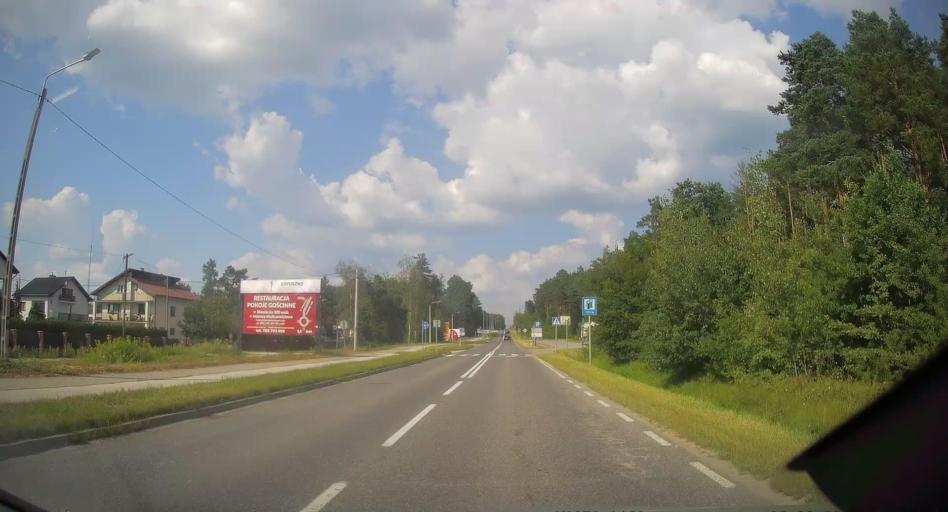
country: PL
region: Swietokrzyskie
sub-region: Powiat kielecki
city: Lopuszno
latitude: 50.9378
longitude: 20.2427
